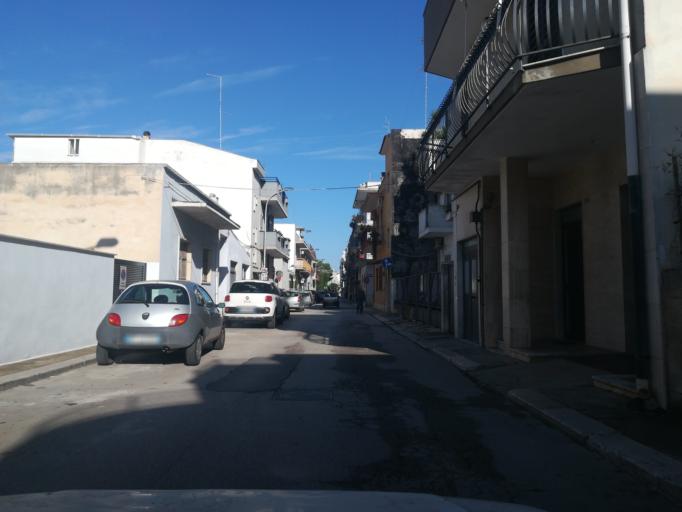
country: IT
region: Apulia
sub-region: Provincia di Bari
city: Modugno
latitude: 41.0783
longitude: 16.7841
